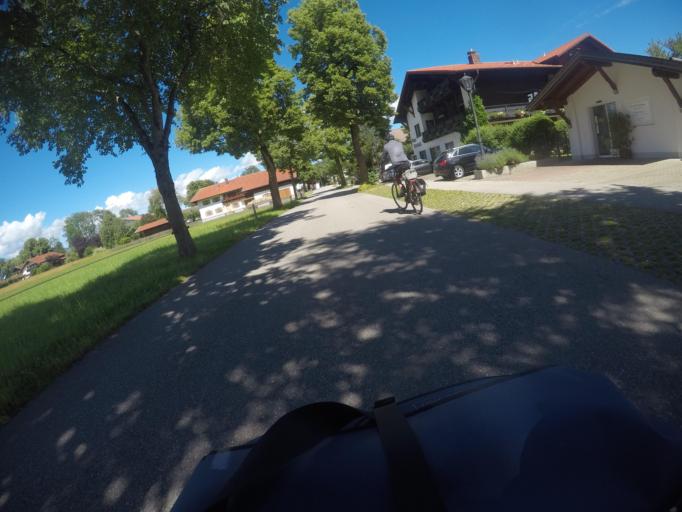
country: DE
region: Bavaria
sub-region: Swabia
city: Schwangau
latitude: 47.5839
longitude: 10.7293
